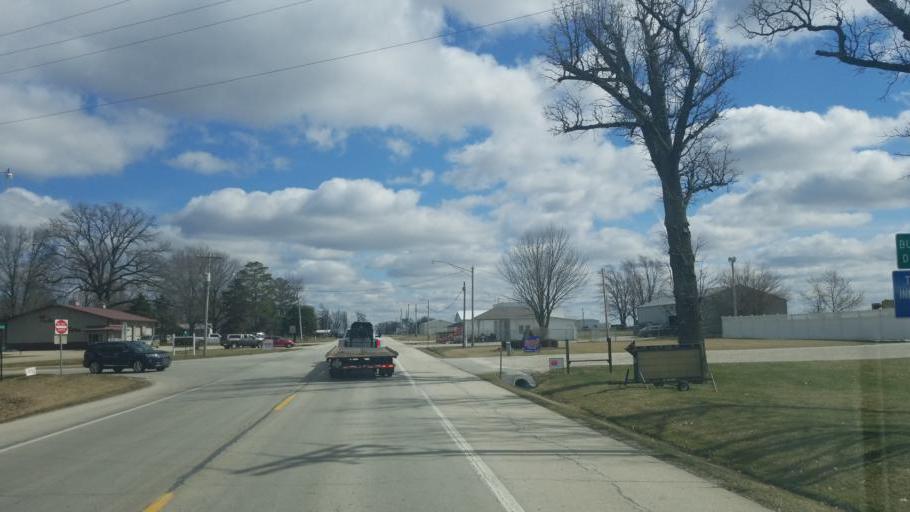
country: US
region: Illinois
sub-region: Douglas County
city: Atwood
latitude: 39.7918
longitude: -88.4610
